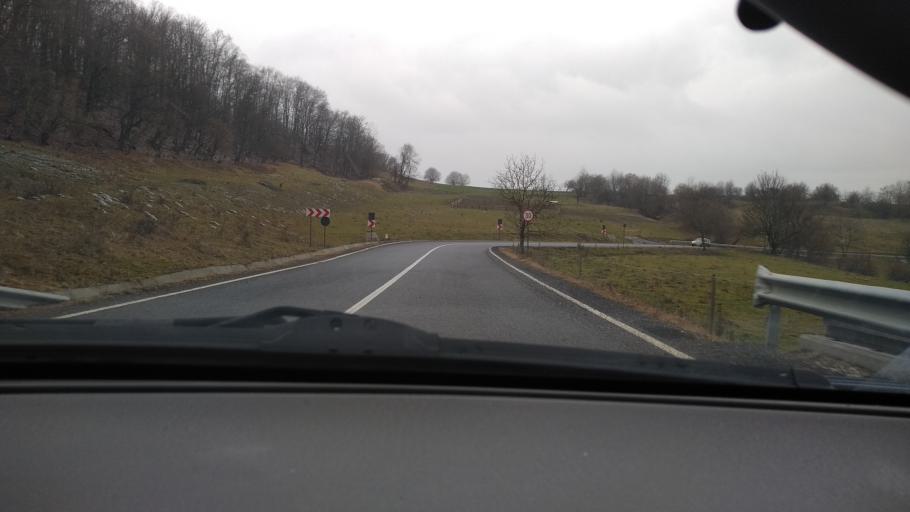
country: RO
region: Mures
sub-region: Comuna Magherani
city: Magherani
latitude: 46.5802
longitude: 24.9472
